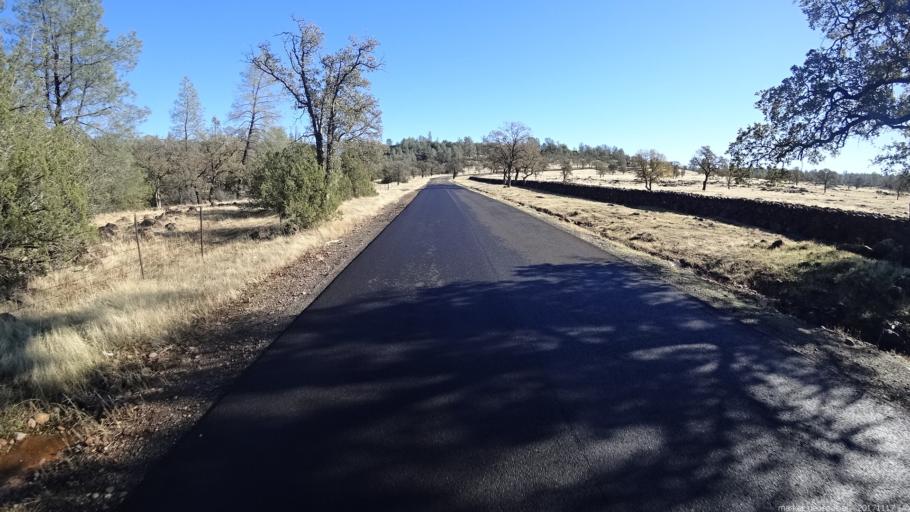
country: US
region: California
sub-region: Shasta County
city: Cottonwood
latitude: 40.4400
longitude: -122.1281
